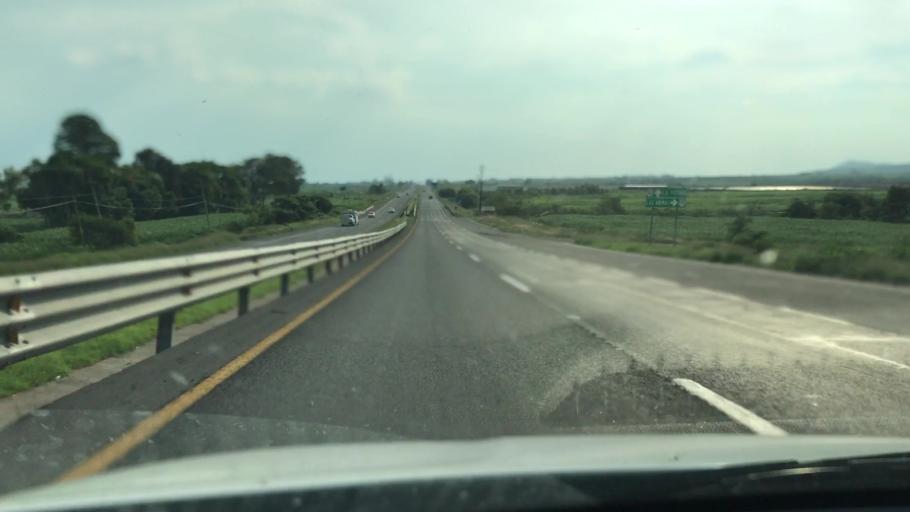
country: MX
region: Guanajuato
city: Penjamo
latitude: 20.3838
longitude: -101.7976
